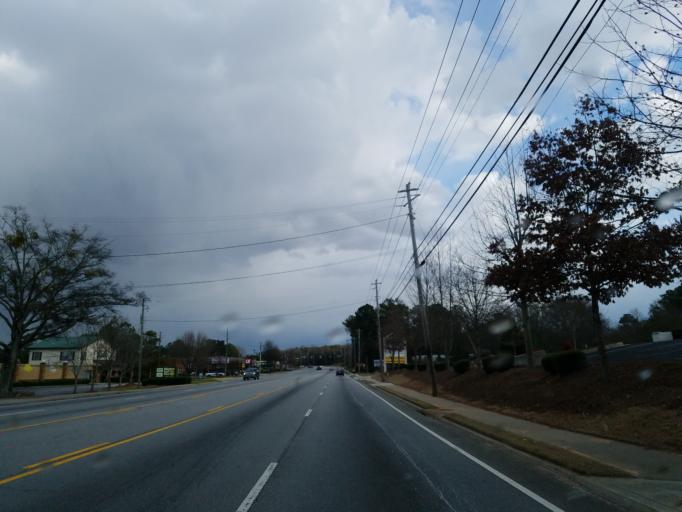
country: US
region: Georgia
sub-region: Henry County
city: Stockbridge
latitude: 33.5489
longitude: -84.2535
